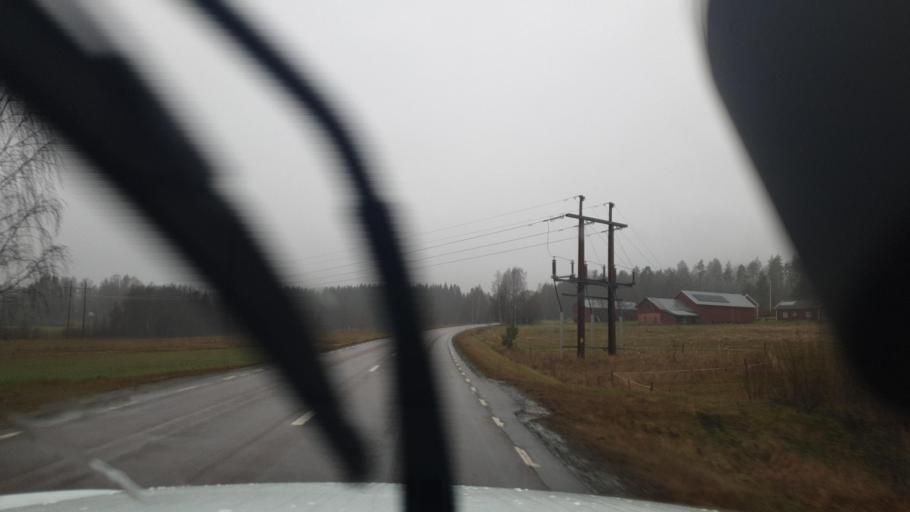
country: SE
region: Vaermland
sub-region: Arvika Kommun
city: Arvika
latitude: 59.6368
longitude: 12.7948
